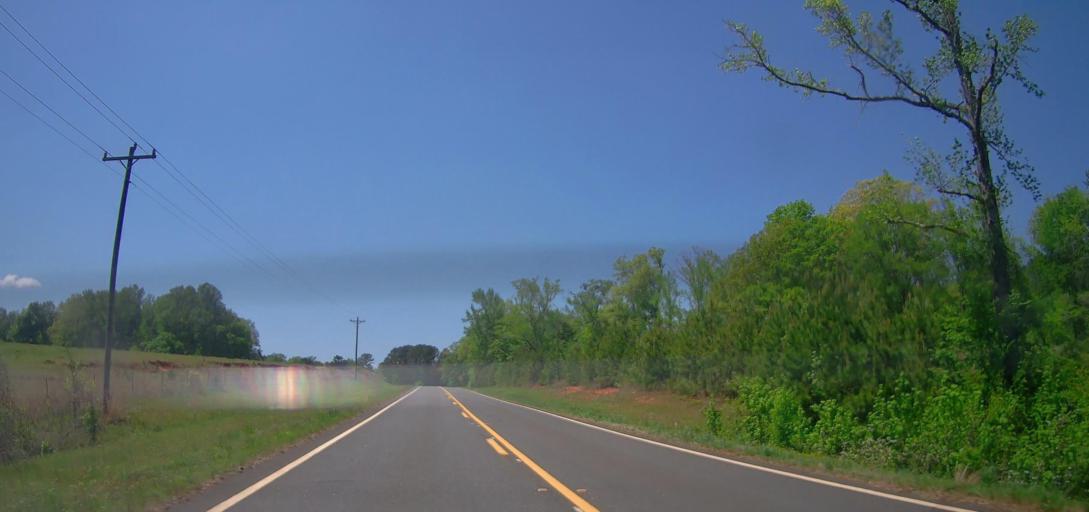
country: US
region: Georgia
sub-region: Jasper County
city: Monticello
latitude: 33.2762
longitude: -83.6149
